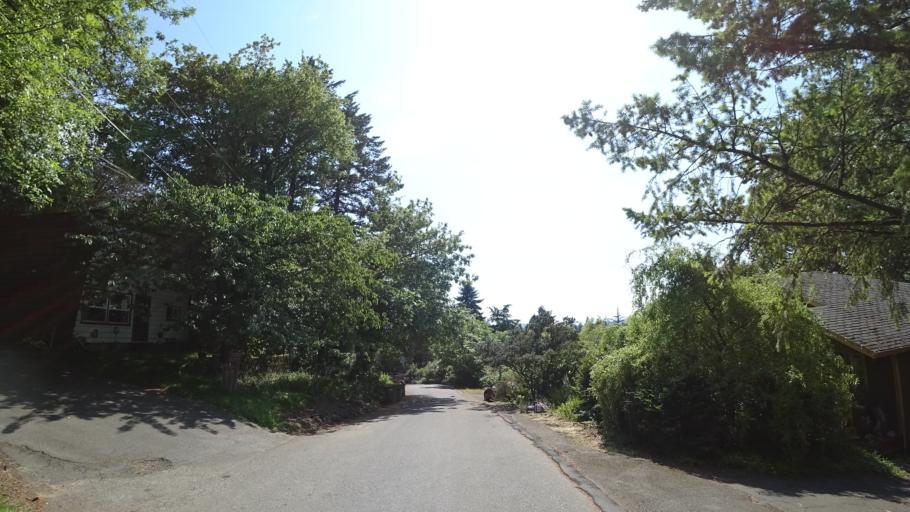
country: US
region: Oregon
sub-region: Washington County
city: Metzger
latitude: 45.4509
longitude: -122.7478
